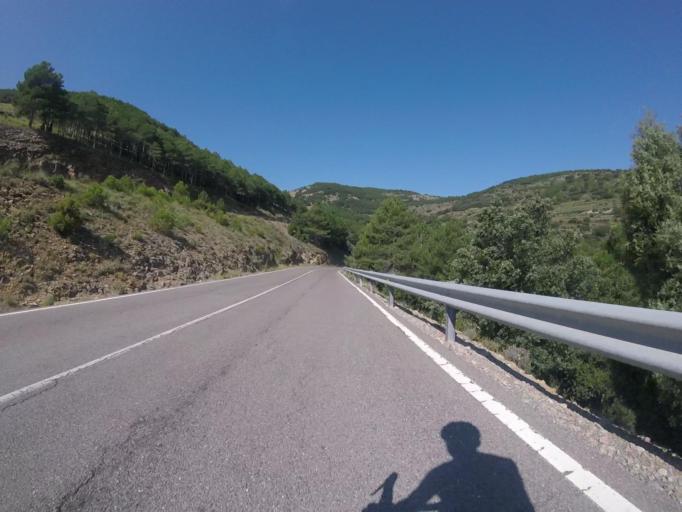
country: ES
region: Valencia
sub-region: Provincia de Castello
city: Benafigos
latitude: 40.2674
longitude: -0.2385
